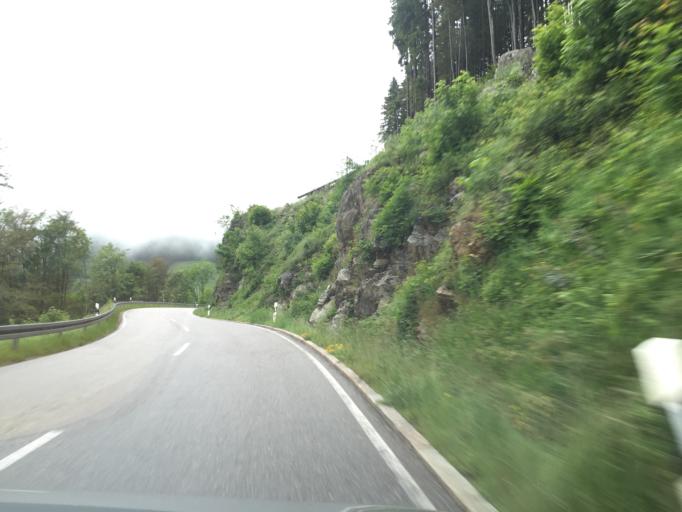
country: DE
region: Baden-Wuerttemberg
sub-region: Freiburg Region
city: Todtnau
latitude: 47.8437
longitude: 7.9301
